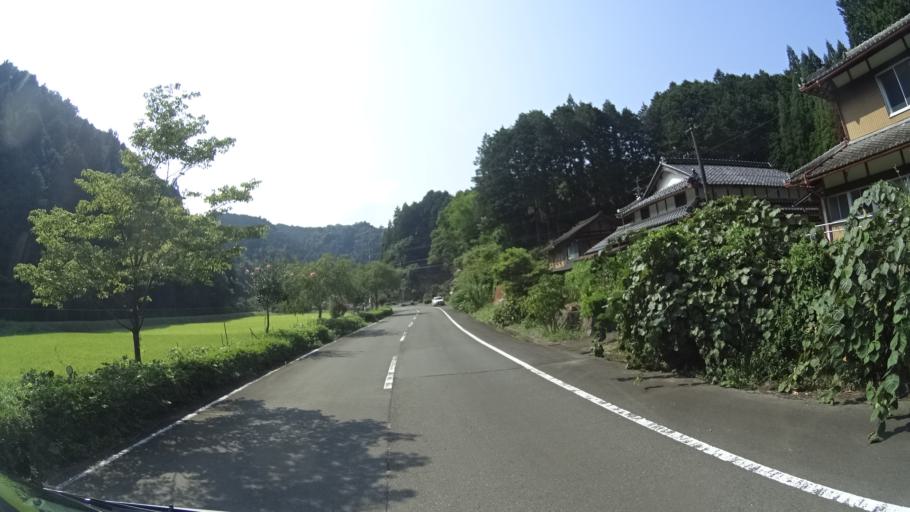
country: JP
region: Kyoto
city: Ayabe
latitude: 35.4028
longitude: 135.2021
